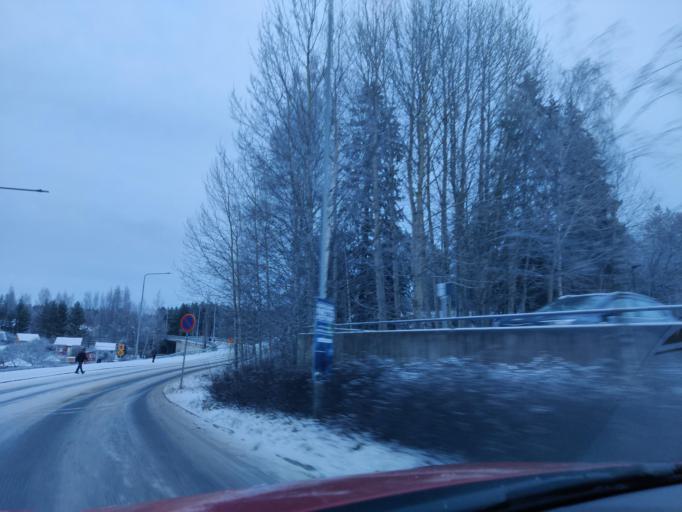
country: FI
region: Pirkanmaa
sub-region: Tampere
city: Tampere
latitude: 61.5022
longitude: 23.8011
